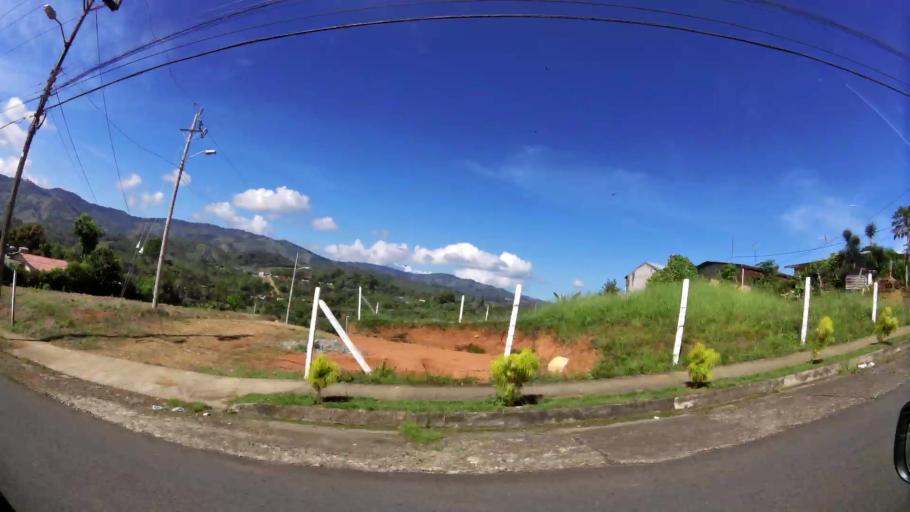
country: CR
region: San Jose
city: San Isidro
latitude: 9.3648
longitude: -83.7128
